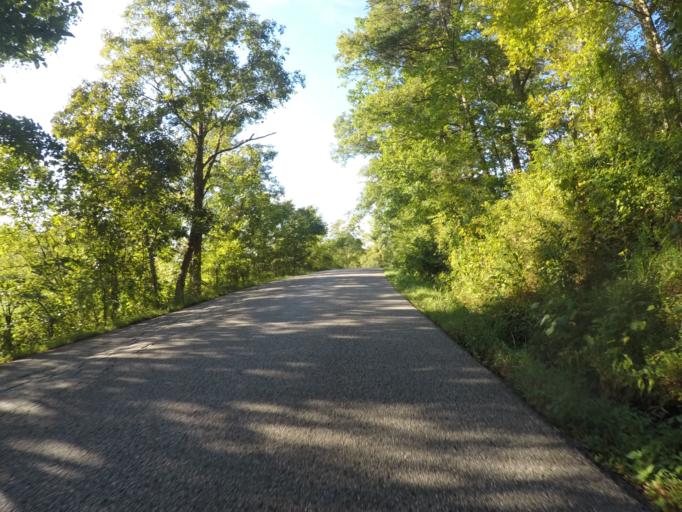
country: US
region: West Virginia
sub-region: Cabell County
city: Huntington
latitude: 38.5051
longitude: -82.4902
